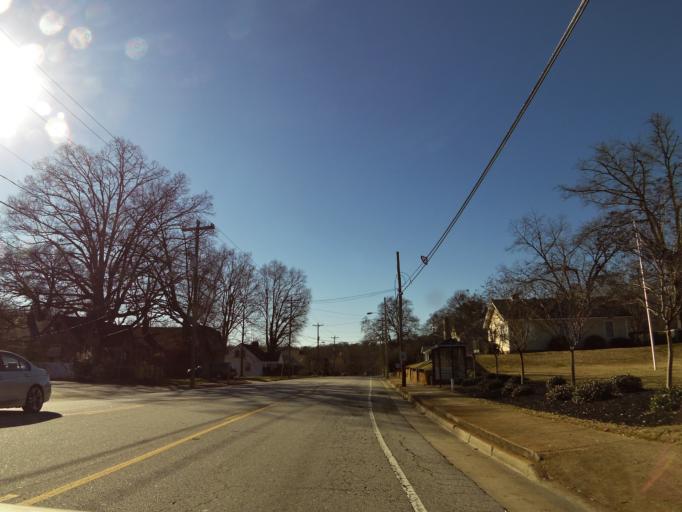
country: US
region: South Carolina
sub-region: Greenville County
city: Greenville
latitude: 34.8507
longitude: -82.3797
